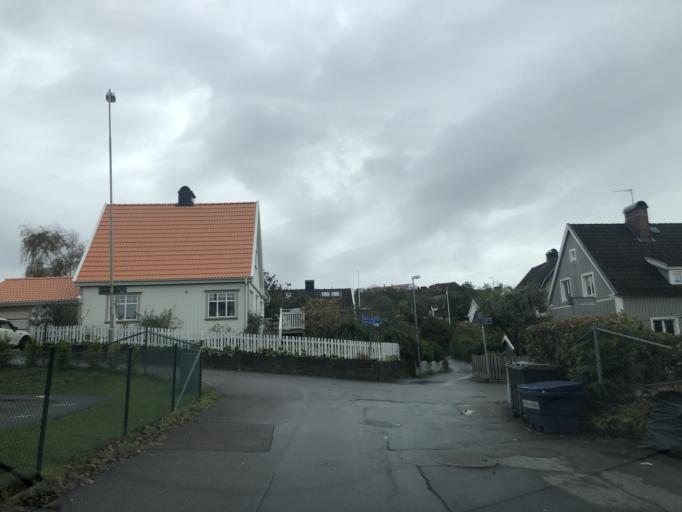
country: SE
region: Vaestra Goetaland
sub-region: Goteborg
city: Majorna
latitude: 57.6751
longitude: 11.8884
